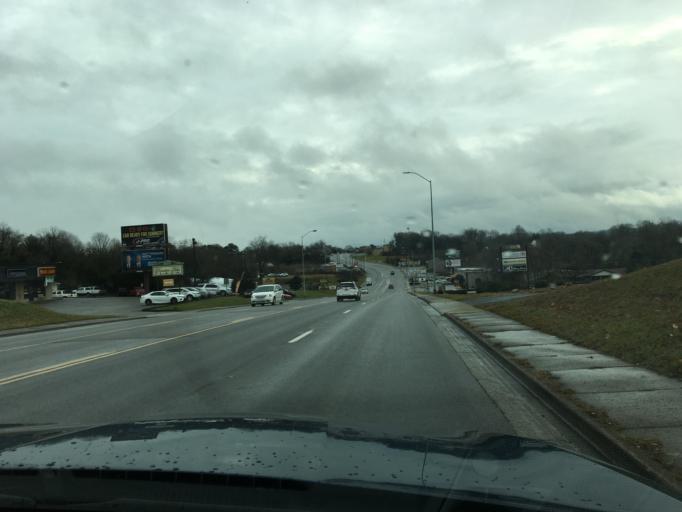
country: US
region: Tennessee
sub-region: McMinn County
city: Athens
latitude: 35.4483
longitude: -84.6065
